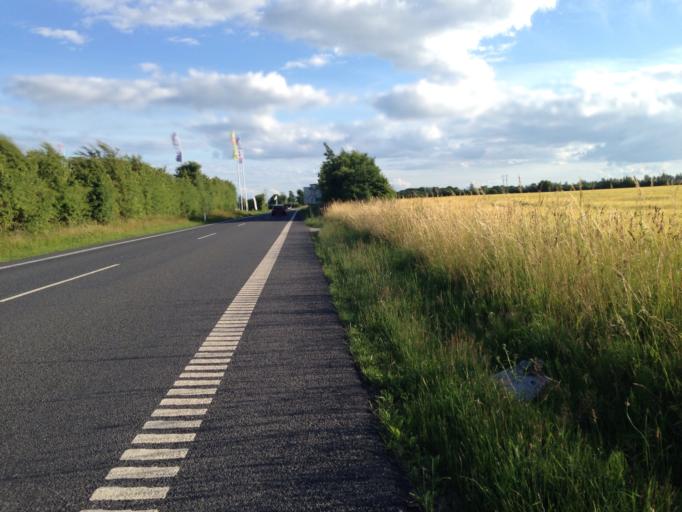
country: DK
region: South Denmark
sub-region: Middelfart Kommune
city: Norre Aby
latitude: 55.4759
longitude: 9.8989
